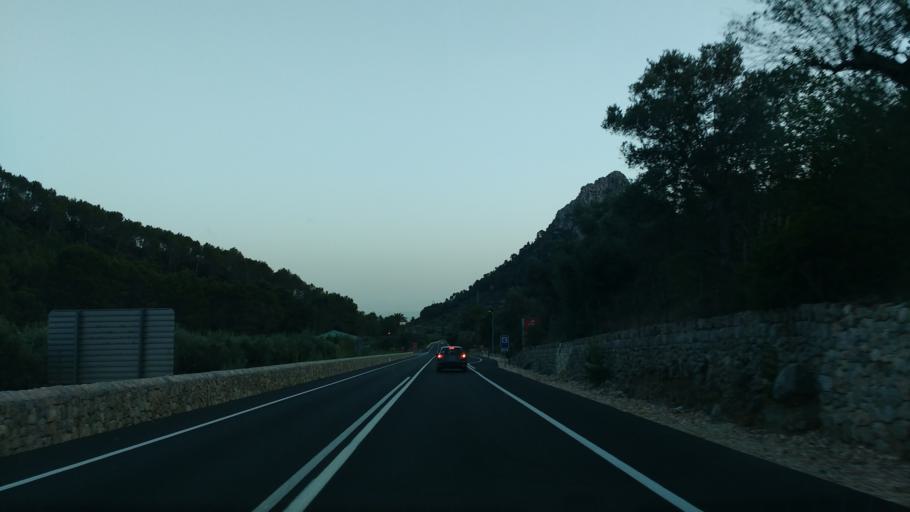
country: ES
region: Balearic Islands
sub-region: Illes Balears
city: Bunyola
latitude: 39.7147
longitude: 2.6903
